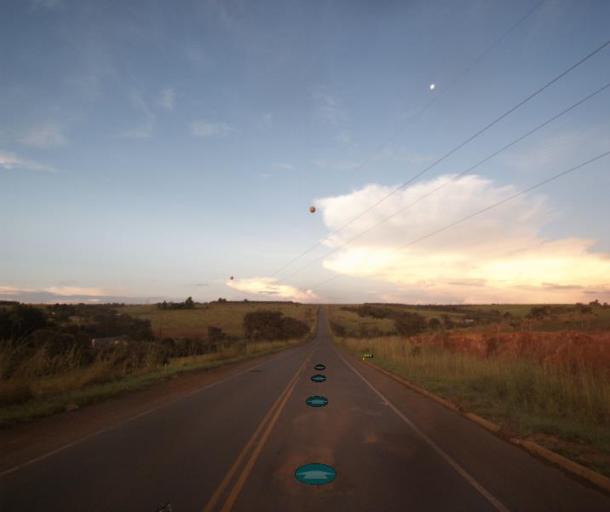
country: BR
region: Goias
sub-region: Pirenopolis
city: Pirenopolis
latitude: -16.0282
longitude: -48.8482
